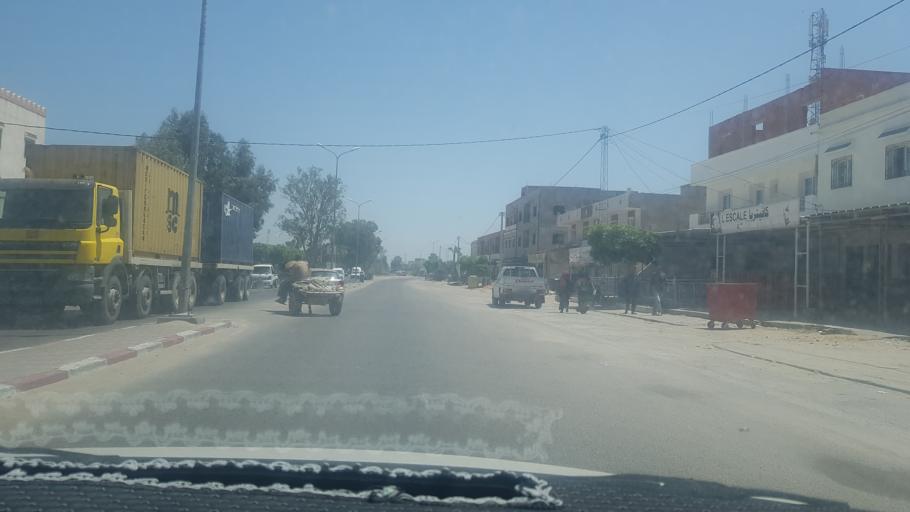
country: TN
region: Al Qayrawan
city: Kairouan
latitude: 35.6155
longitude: 9.9267
